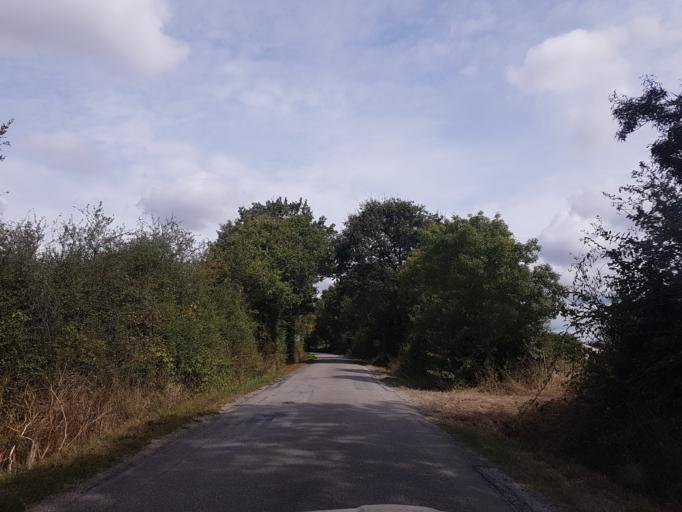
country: FR
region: Pays de la Loire
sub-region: Departement de la Loire-Atlantique
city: Petit-Mars
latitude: 47.3938
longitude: -1.4290
